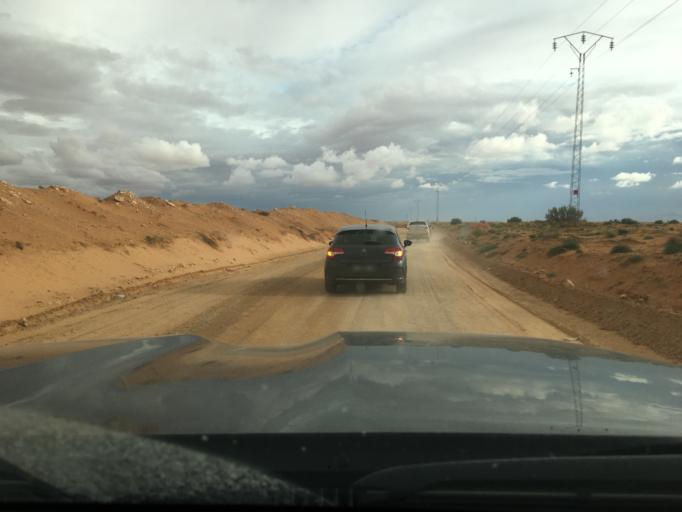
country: TN
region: Madanin
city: Medenine
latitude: 33.2724
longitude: 10.5659
